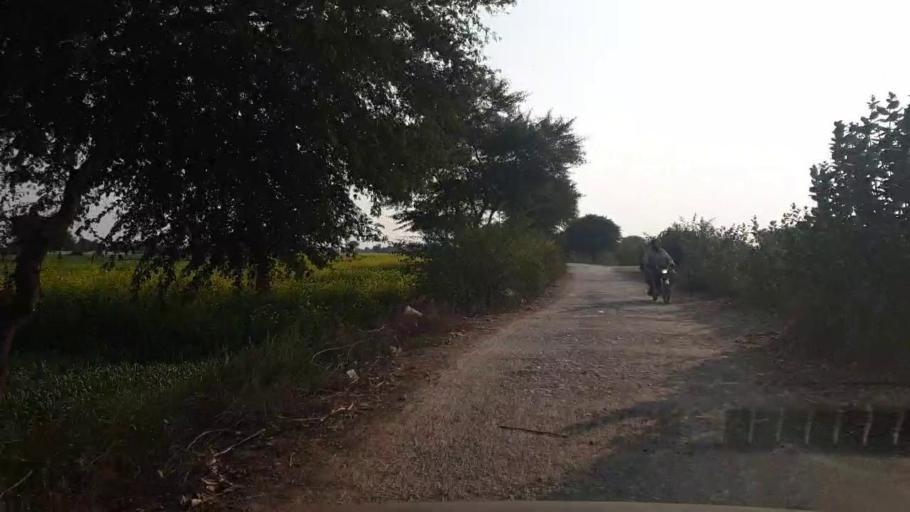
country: PK
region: Sindh
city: Bhit Shah
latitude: 25.7793
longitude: 68.4682
